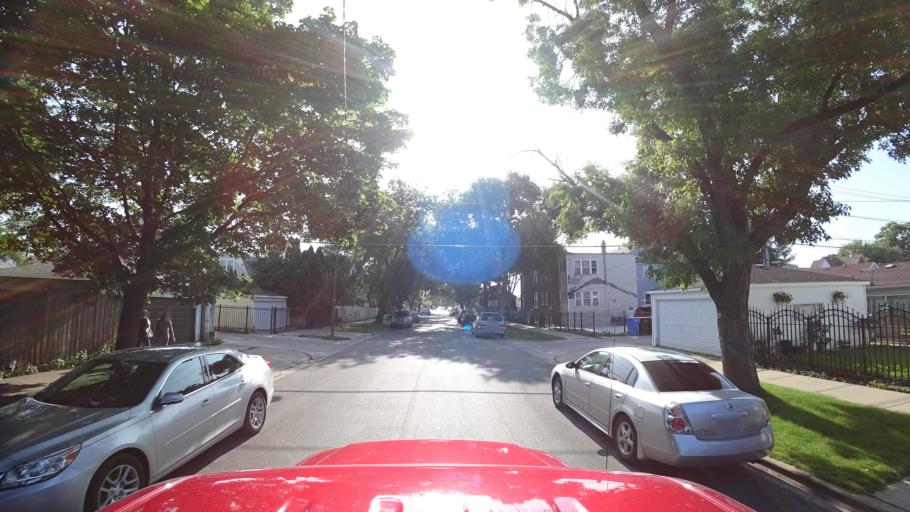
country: US
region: Illinois
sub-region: Cook County
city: Hometown
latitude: 41.7880
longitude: -87.7055
